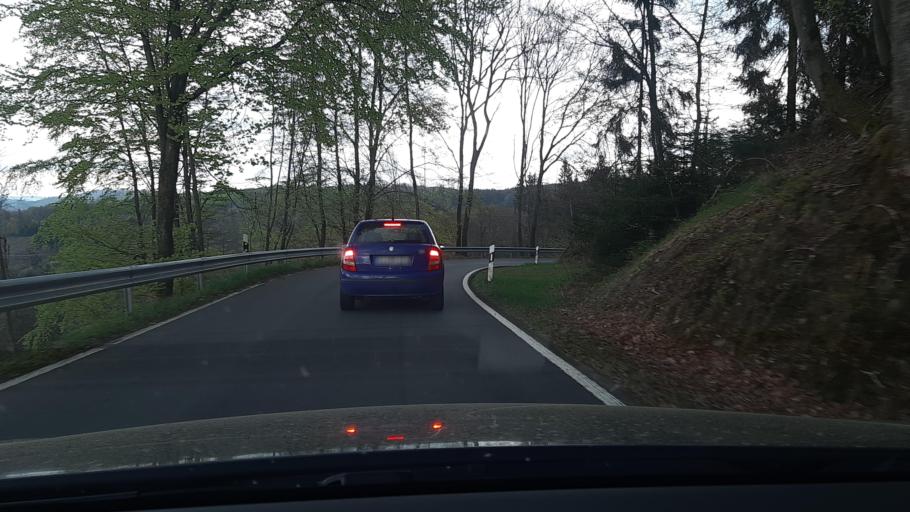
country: DE
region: North Rhine-Westphalia
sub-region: Regierungsbezirk Arnsberg
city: Bad Laasphe
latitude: 50.8886
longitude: 8.3865
